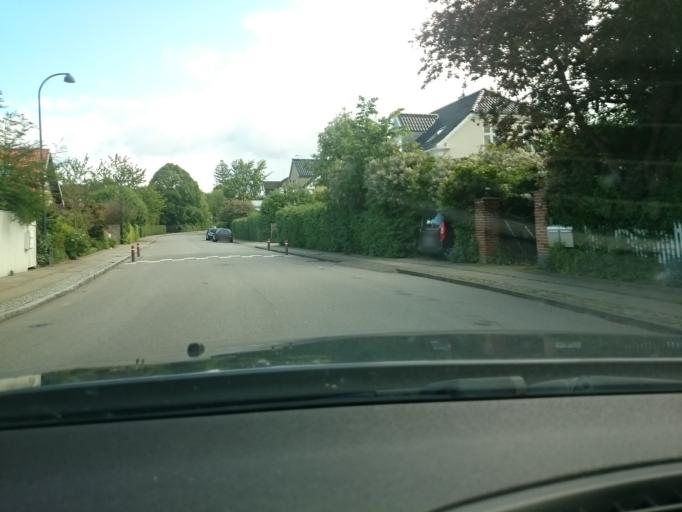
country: DK
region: Capital Region
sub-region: Gentofte Kommune
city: Charlottenlund
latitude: 55.7517
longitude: 12.5608
